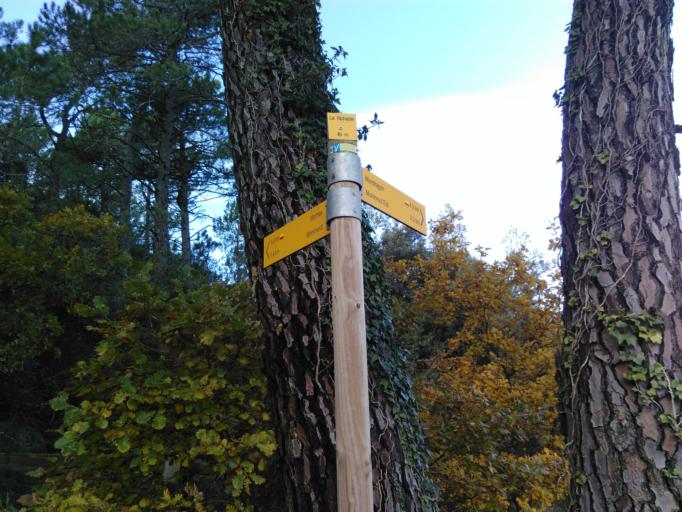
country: FR
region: Provence-Alpes-Cote d'Azur
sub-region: Departement du Vaucluse
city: Mornas
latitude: 44.2250
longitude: 4.7523
